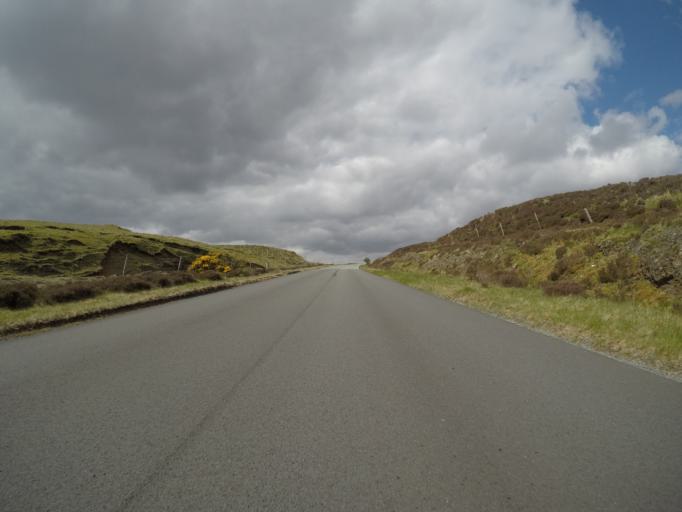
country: GB
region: Scotland
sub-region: Highland
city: Isle of Skye
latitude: 57.3078
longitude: -6.3163
